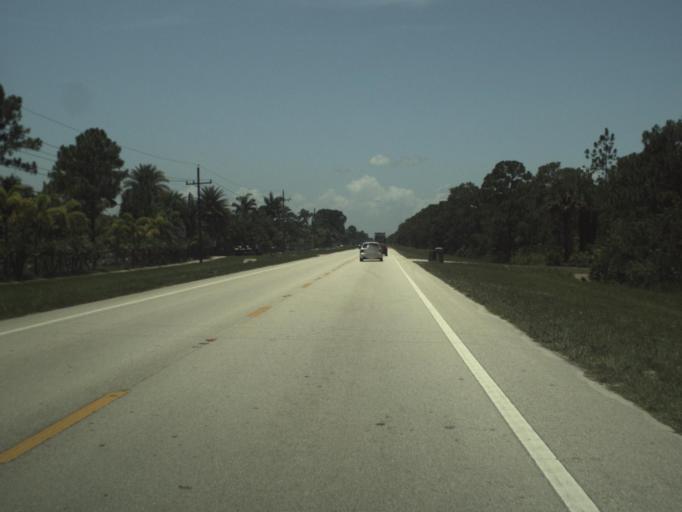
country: US
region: Florida
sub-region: Martin County
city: Palm City
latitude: 27.1617
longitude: -80.3460
